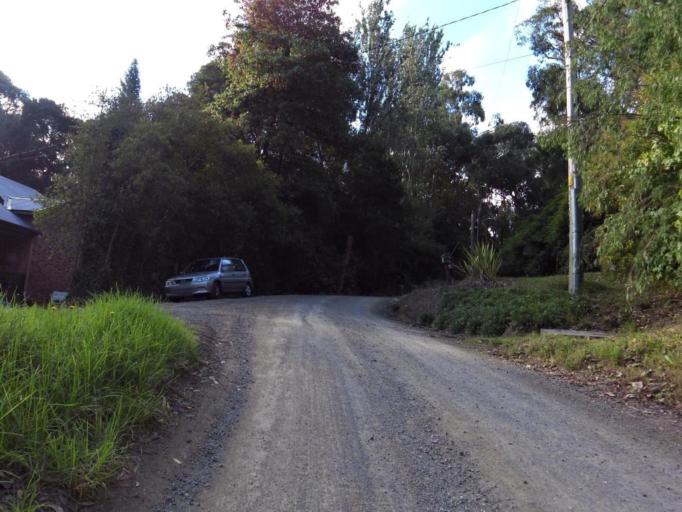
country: AU
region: Victoria
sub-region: Yarra Ranges
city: Mount Evelyn
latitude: -37.7892
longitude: 145.3847
